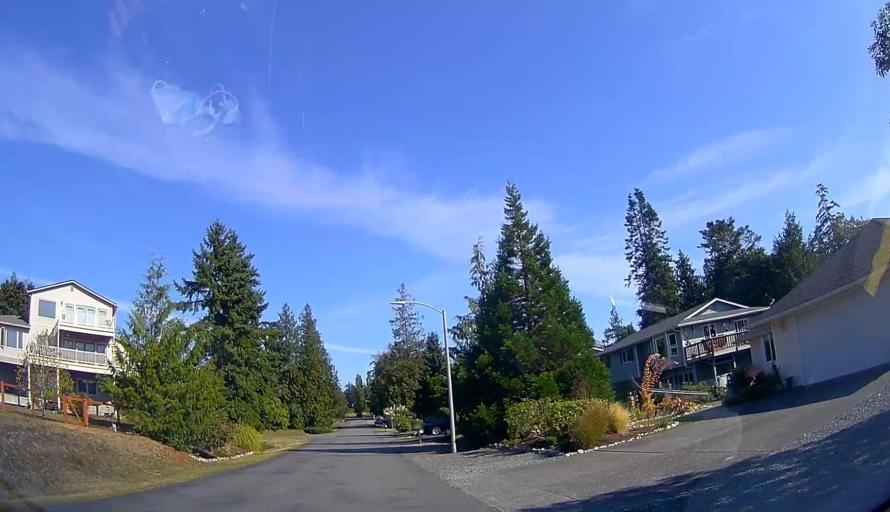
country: US
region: Washington
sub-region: Island County
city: Camano
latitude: 48.1824
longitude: -122.5312
